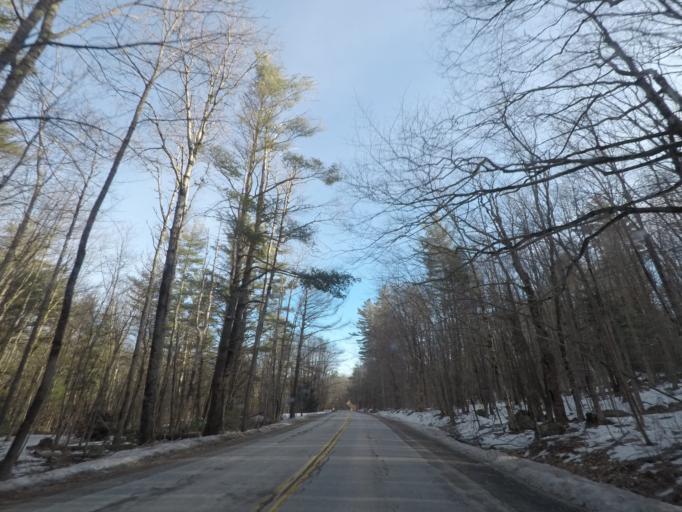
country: US
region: New York
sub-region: Rensselaer County
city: Hoosick Falls
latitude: 42.7416
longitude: -73.4032
